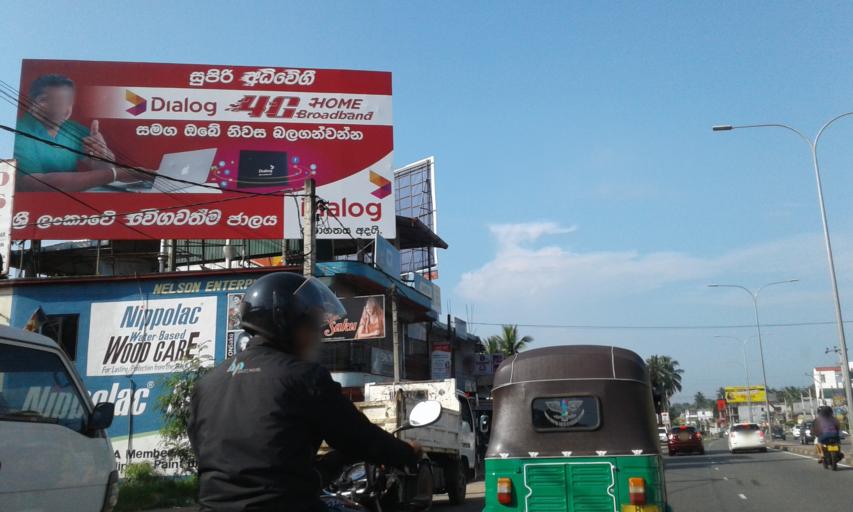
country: LK
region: Western
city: Gampaha
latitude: 7.0347
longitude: 79.9905
